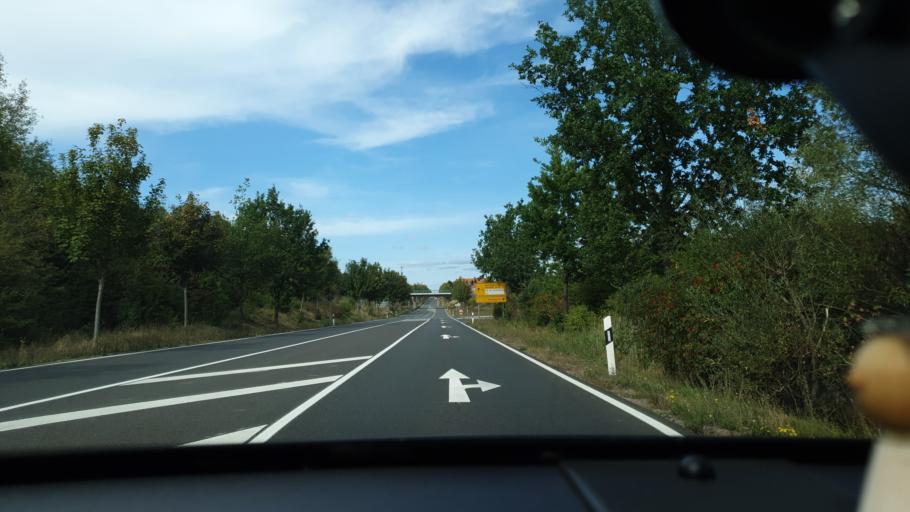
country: DE
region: Saxony
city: Eilenburg
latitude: 51.4478
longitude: 12.6132
